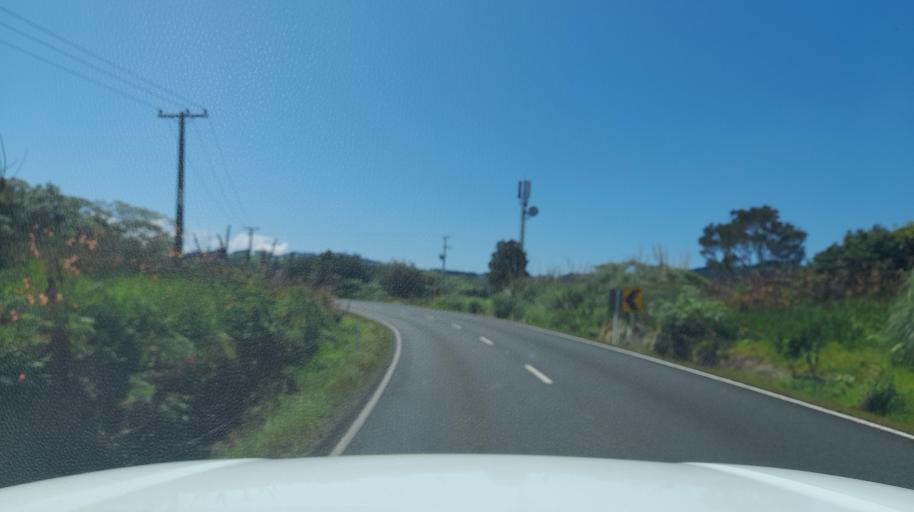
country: NZ
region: Northland
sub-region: Far North District
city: Taipa
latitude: -35.0369
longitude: 173.4905
